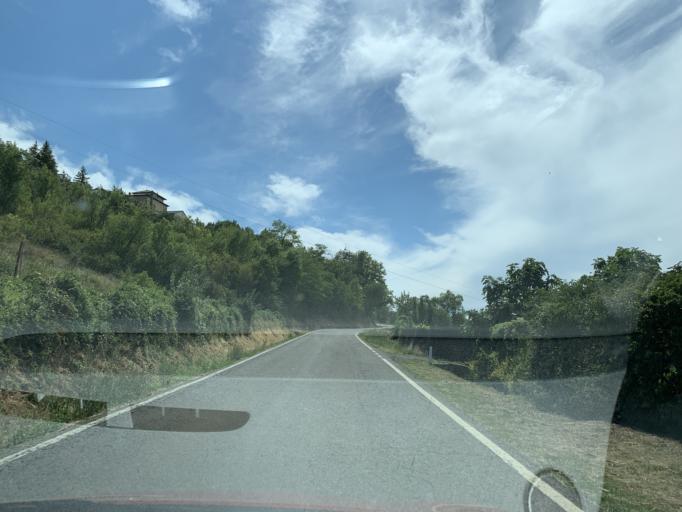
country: ES
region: Aragon
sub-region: Provincia de Huesca
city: Jaca
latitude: 42.5761
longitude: -0.5551
